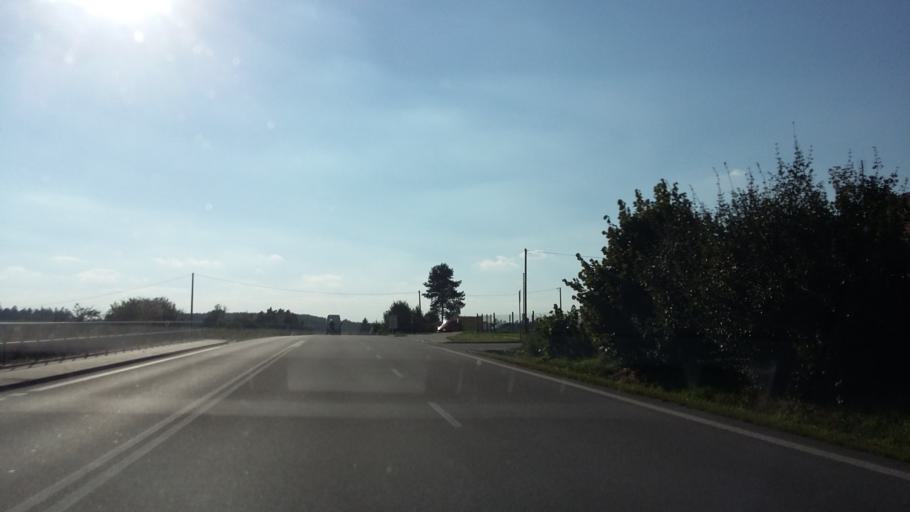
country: CZ
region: South Moravian
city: Troubsko
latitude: 49.1900
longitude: 16.4526
